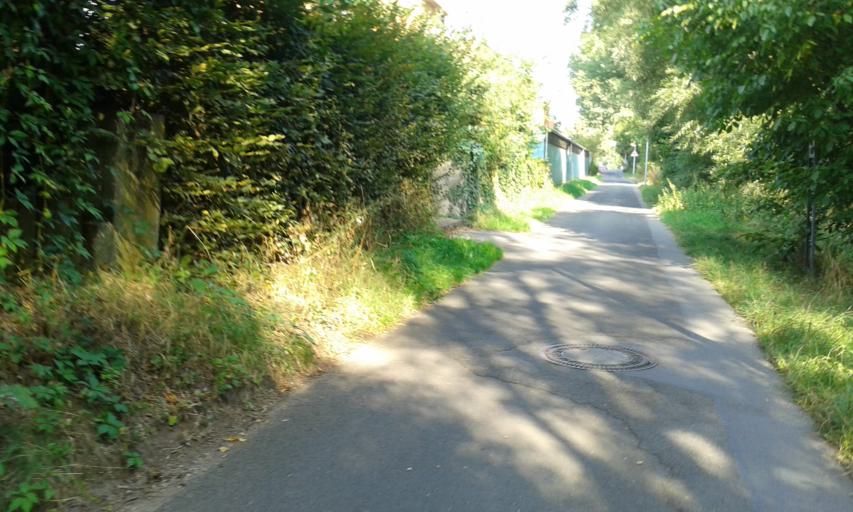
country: DE
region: Bavaria
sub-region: Upper Franconia
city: Hallstadt
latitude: 49.9041
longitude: 10.8646
